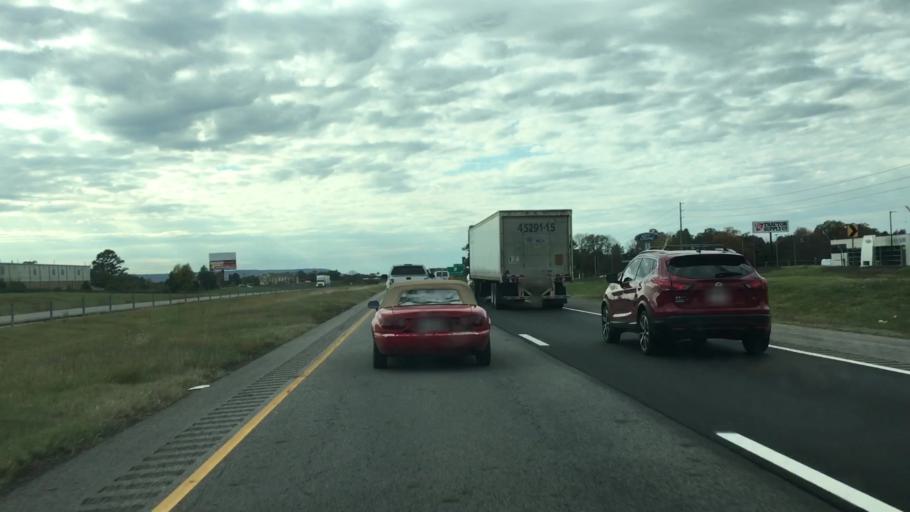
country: US
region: Arkansas
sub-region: Conway County
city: Morrilton
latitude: 35.1742
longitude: -92.7093
